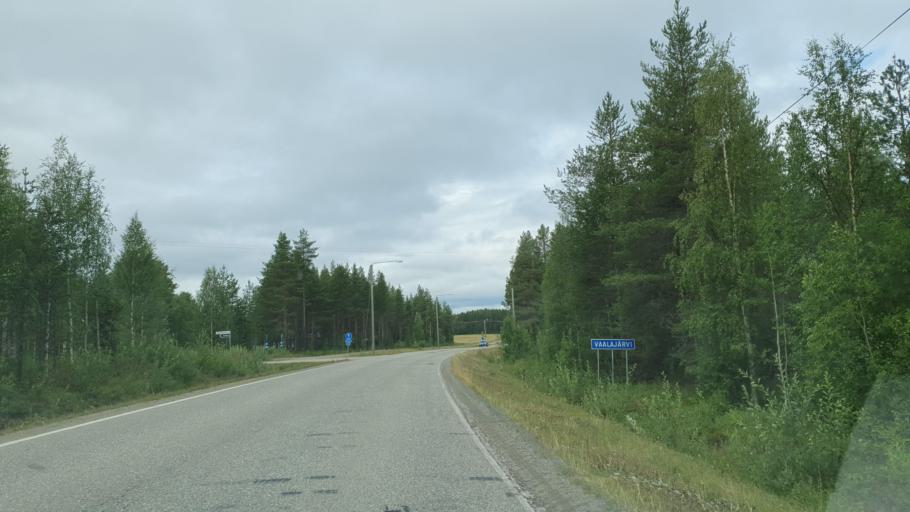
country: FI
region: Lapland
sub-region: Pohjois-Lappi
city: Sodankylae
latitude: 67.4163
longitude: 26.2416
